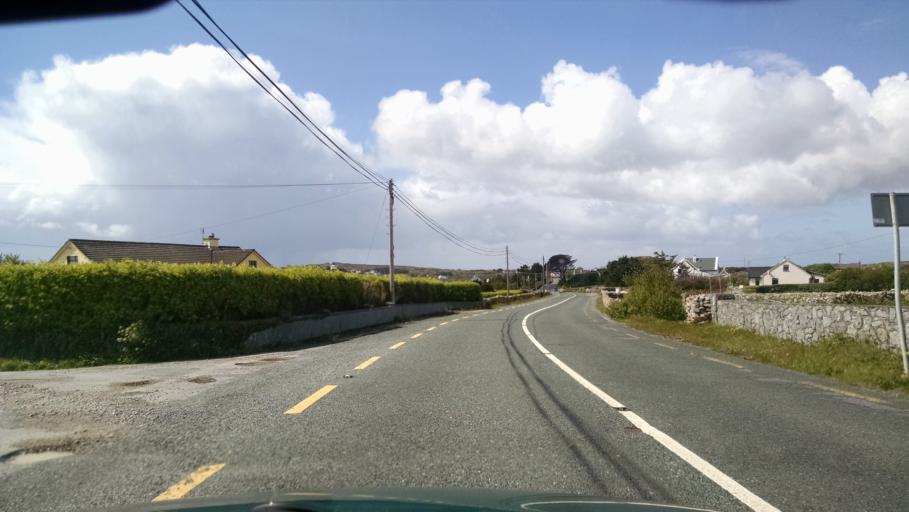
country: IE
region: Connaught
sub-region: County Galway
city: Oughterard
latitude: 53.2830
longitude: -9.5692
